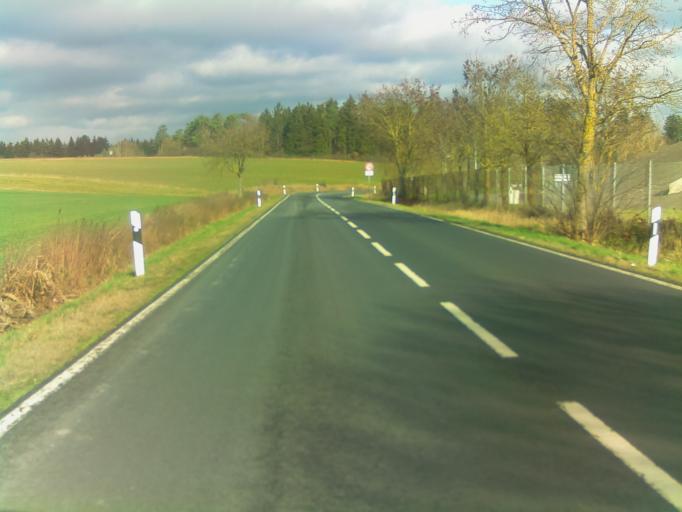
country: DE
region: Thuringia
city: Reurieth
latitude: 50.4034
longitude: 10.6714
